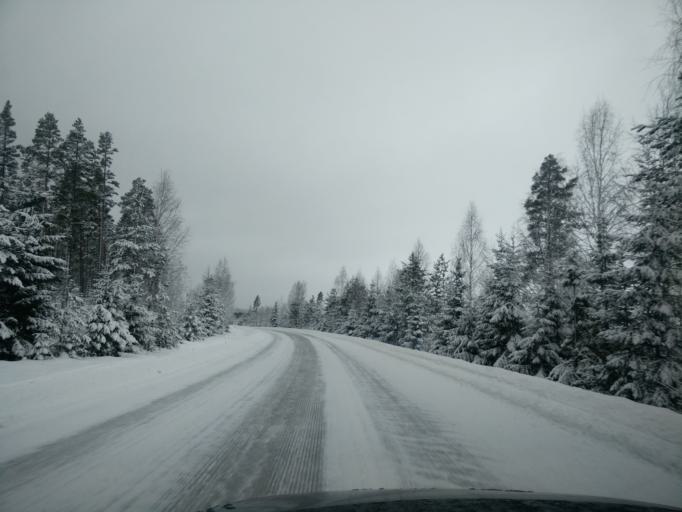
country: SE
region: Vaesternorrland
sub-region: Ange Kommun
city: Ange
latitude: 62.3935
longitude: 15.4110
